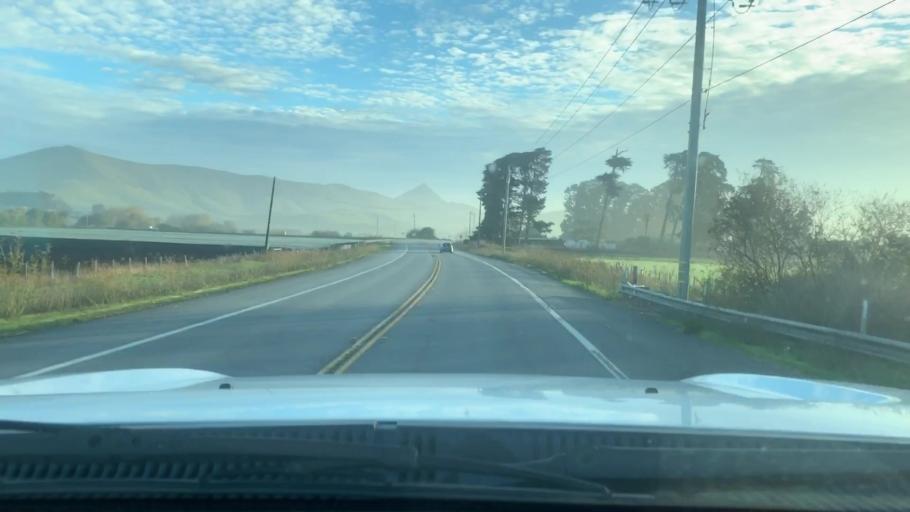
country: US
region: California
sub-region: San Luis Obispo County
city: Los Osos
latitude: 35.2990
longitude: -120.7807
